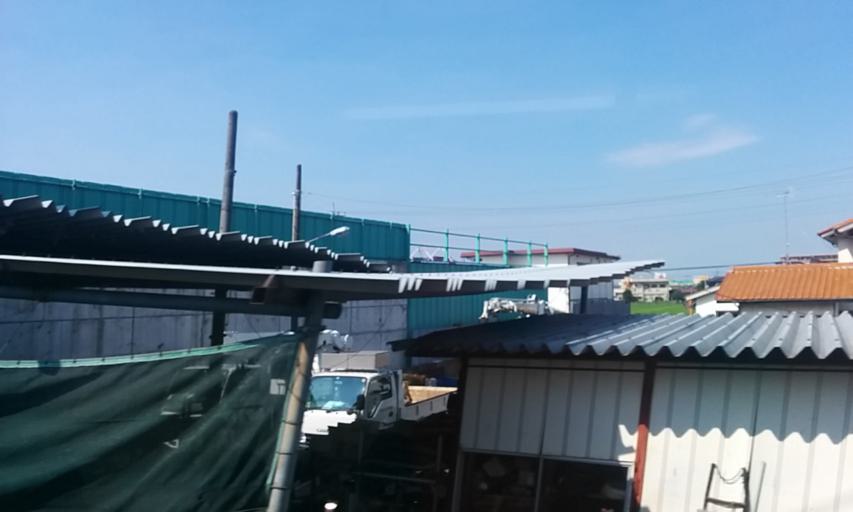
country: JP
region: Saitama
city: Kukichuo
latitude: 36.0823
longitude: 139.6751
